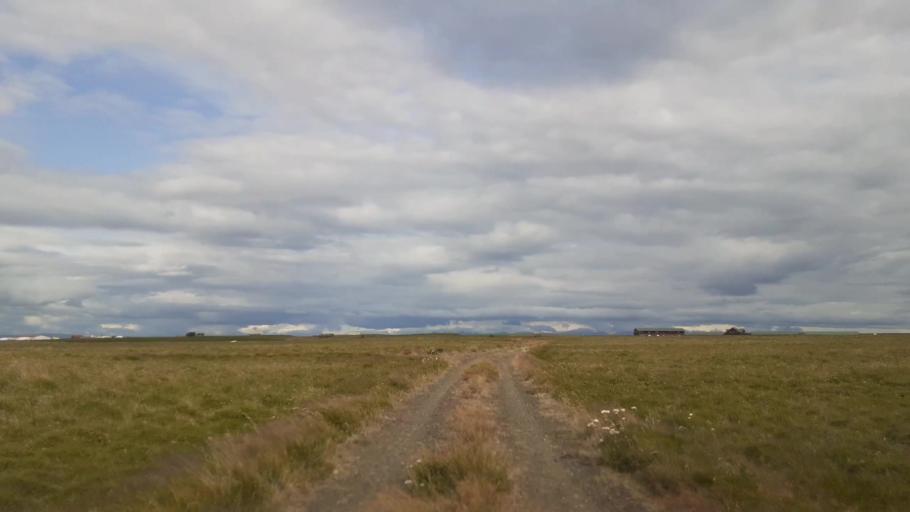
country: IS
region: South
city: Vestmannaeyjar
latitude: 63.7749
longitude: -20.3001
